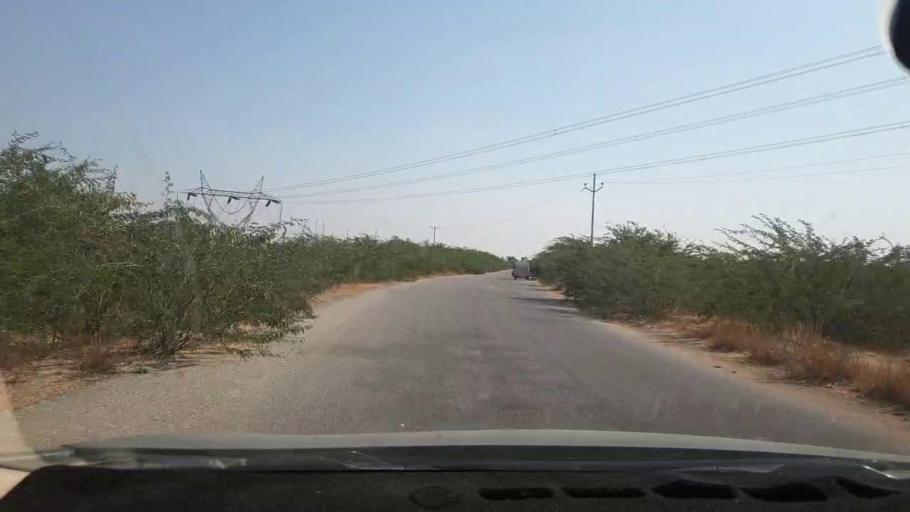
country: PK
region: Sindh
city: Malir Cantonment
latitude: 25.1435
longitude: 67.1927
